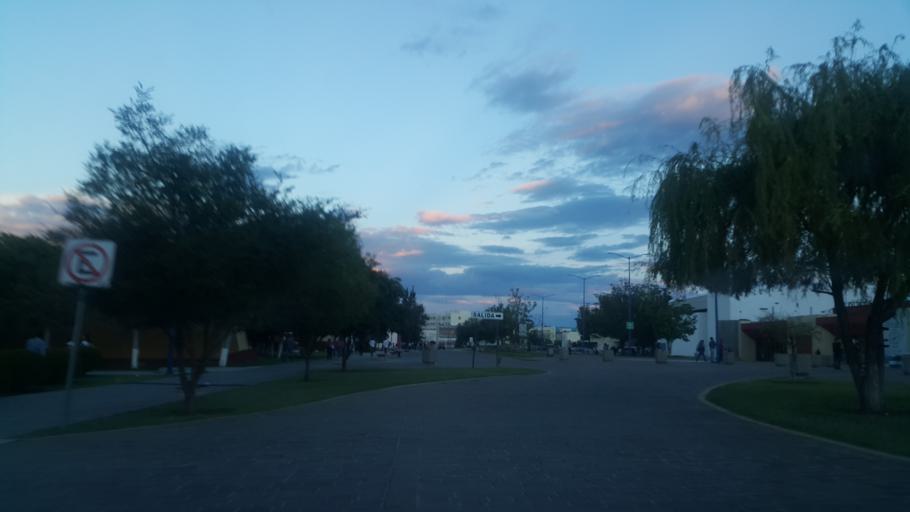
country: MX
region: Guanajuato
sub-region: Leon
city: Ladrilleras del Refugio
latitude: 21.0638
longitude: -101.5819
